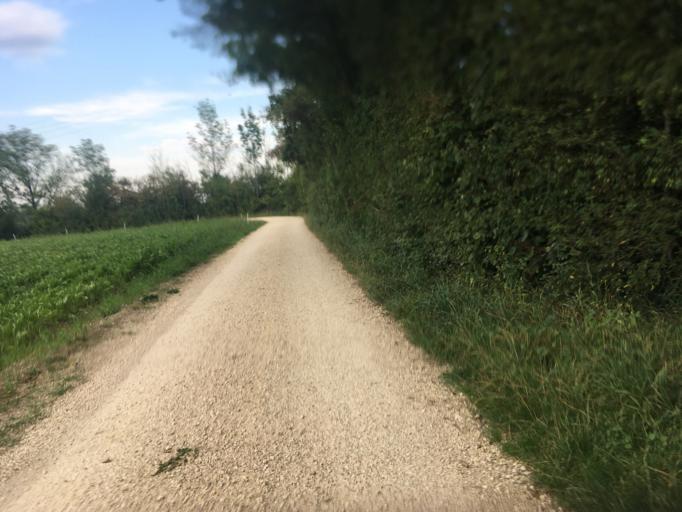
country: CH
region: Solothurn
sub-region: Bezirk Lebern
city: Selzach
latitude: 47.2026
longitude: 7.4828
